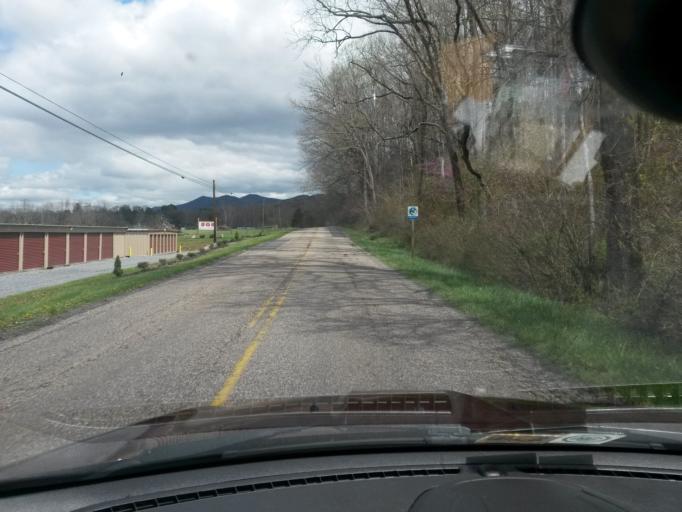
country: US
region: Virginia
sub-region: City of Buena Vista
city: Buena Vista
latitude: 37.7068
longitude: -79.3767
